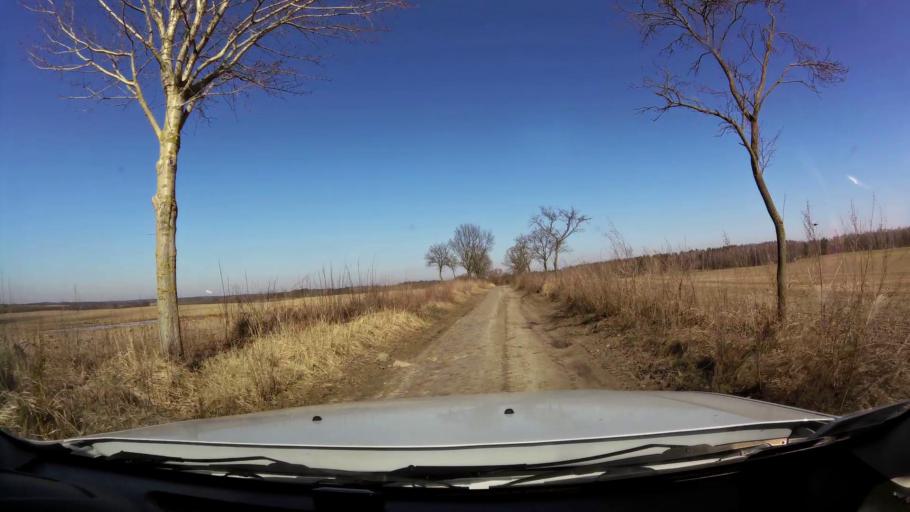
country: PL
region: West Pomeranian Voivodeship
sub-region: Powiat gryfinski
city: Banie
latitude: 53.1471
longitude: 14.6355
